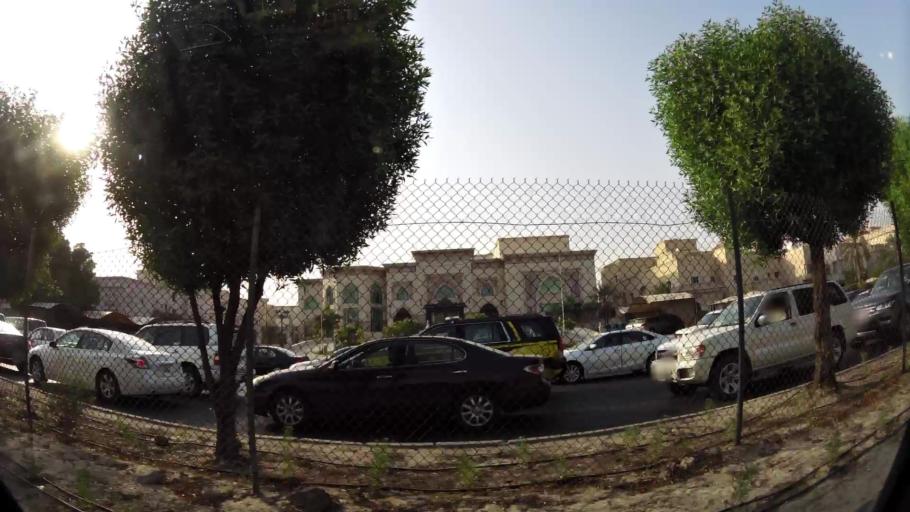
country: KW
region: Muhafazat Hawalli
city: Hawalli
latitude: 29.3210
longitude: 47.9970
